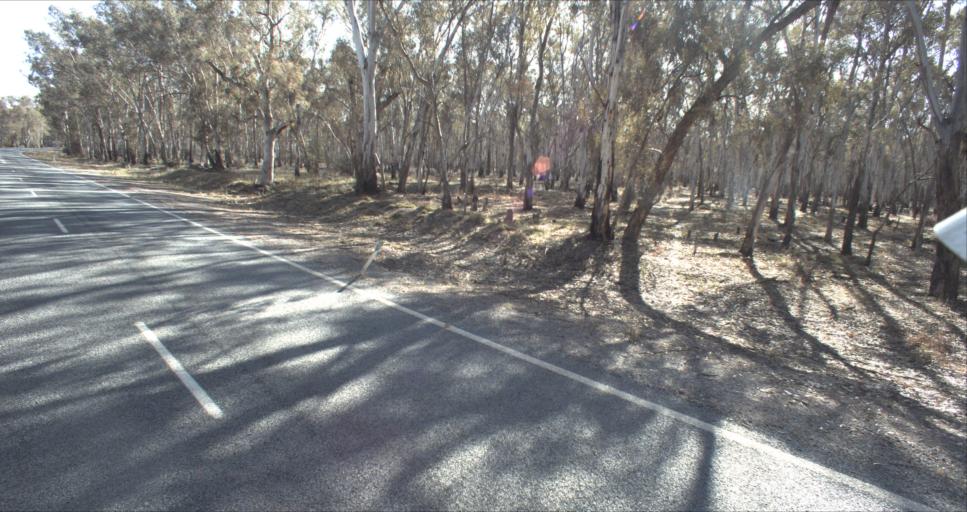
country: AU
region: New South Wales
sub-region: Leeton
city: Leeton
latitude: -34.6286
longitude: 146.3775
